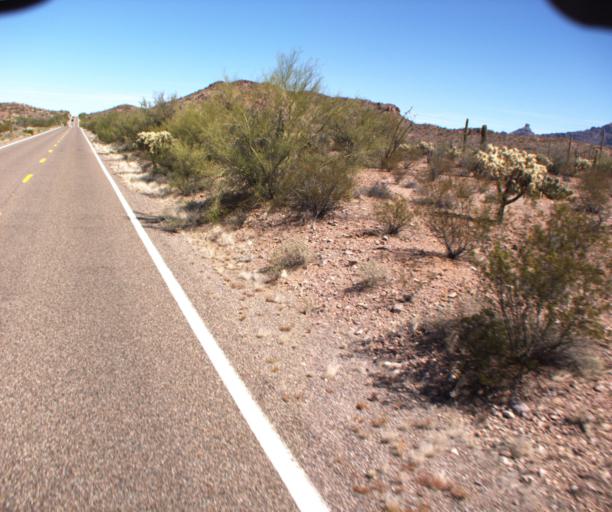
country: MX
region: Sonora
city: Sonoyta
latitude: 32.0771
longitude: -112.7805
